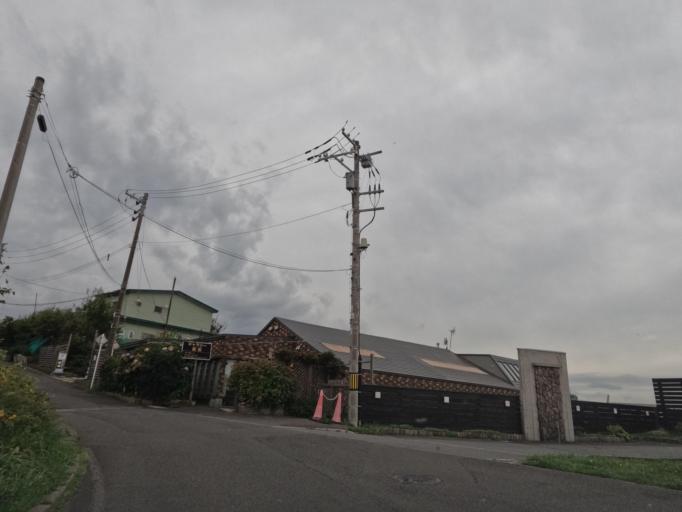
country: JP
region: Hokkaido
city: Muroran
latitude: 42.3377
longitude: 140.9326
